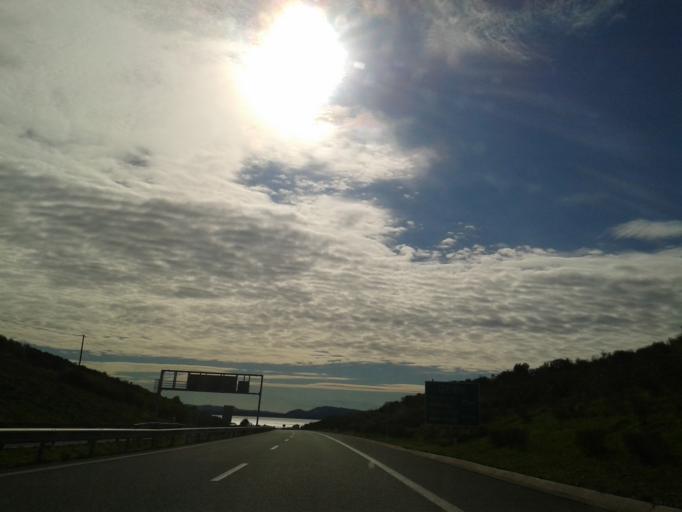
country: GR
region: West Greece
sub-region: Nomos Aitolias kai Akarnanias
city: Fitiai
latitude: 38.6894
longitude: 21.2160
